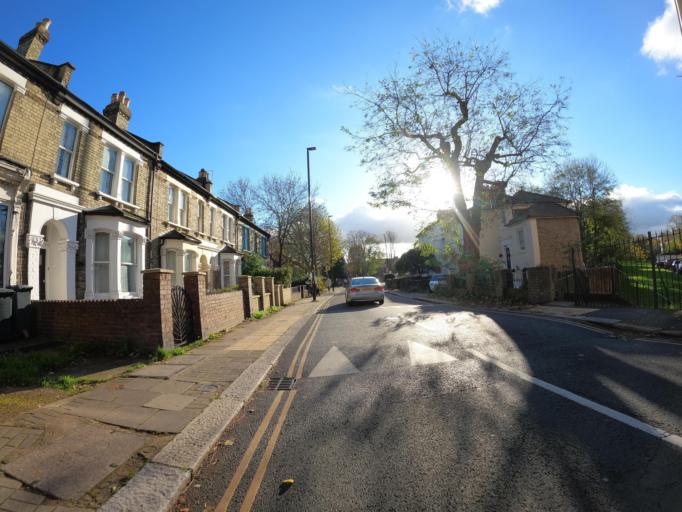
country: GB
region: England
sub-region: Greater London
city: Brentford
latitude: 51.4875
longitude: -0.3078
